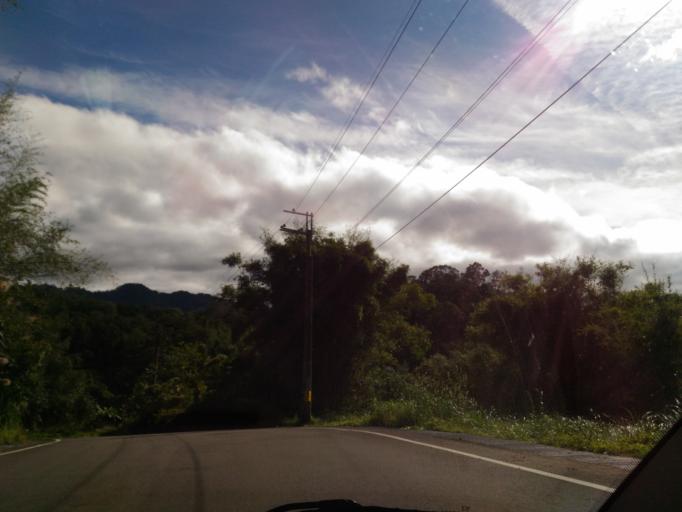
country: TW
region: Taiwan
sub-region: Hsinchu
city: Hsinchu
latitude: 24.7101
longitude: 121.0716
